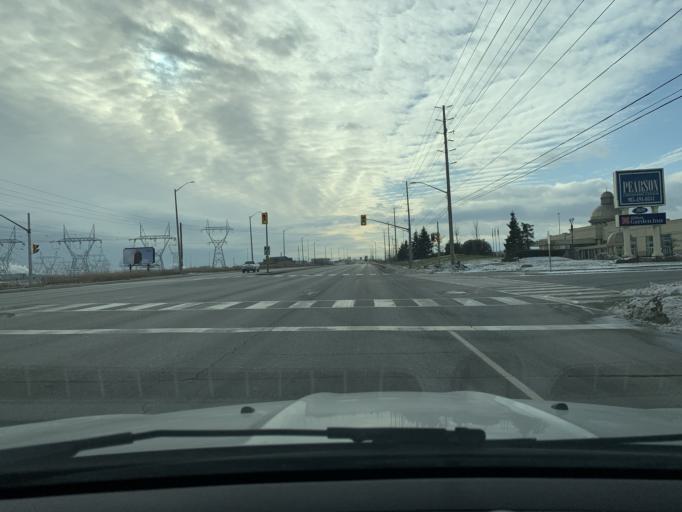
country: CA
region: Ontario
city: Brampton
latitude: 43.7225
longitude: -79.6706
